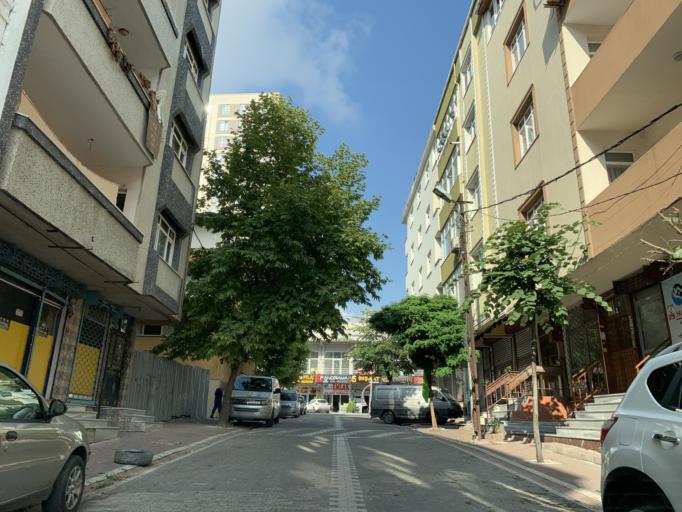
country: TR
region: Istanbul
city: Esenyurt
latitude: 41.0262
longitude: 28.6815
